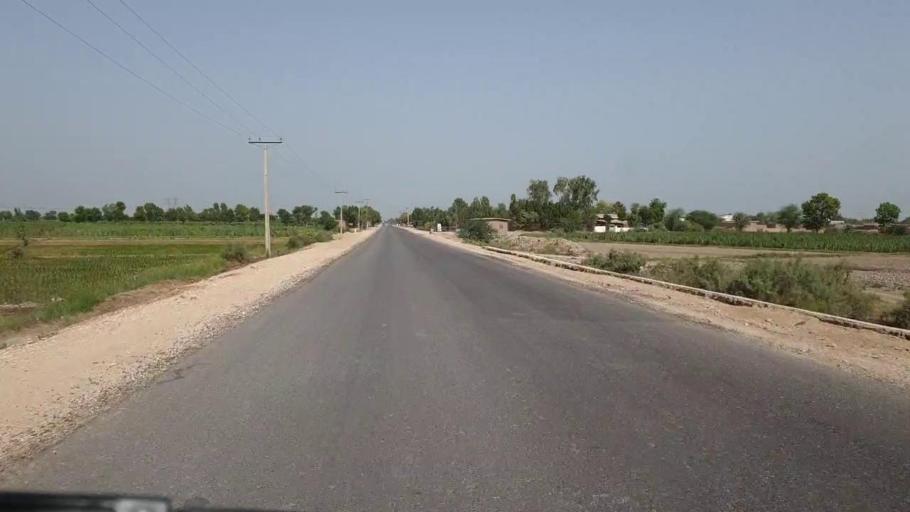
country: PK
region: Sindh
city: Sakrand
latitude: 26.2591
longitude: 68.1886
